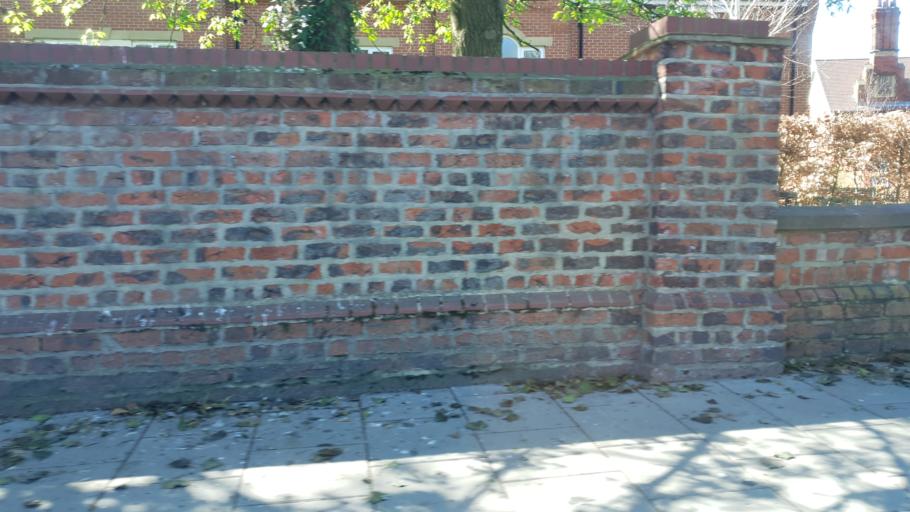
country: GB
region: England
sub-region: Middlesbrough
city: Middlesbrough
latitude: 54.5549
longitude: -1.2460
